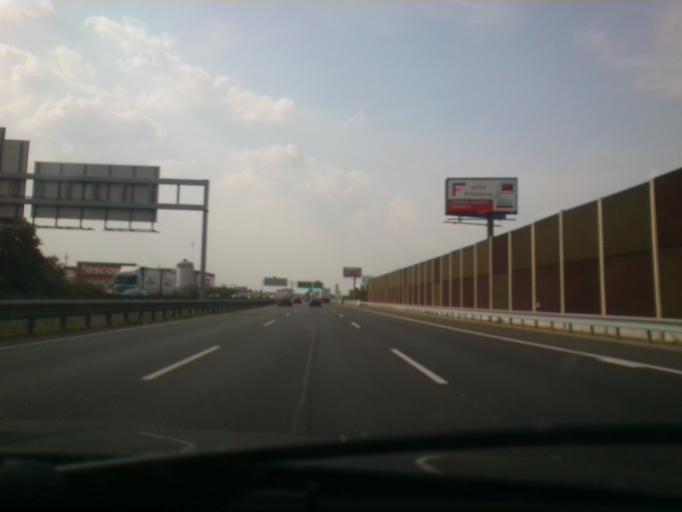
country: CZ
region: Central Bohemia
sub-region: Okres Praha-Zapad
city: Pruhonice
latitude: 49.9881
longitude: 14.5967
